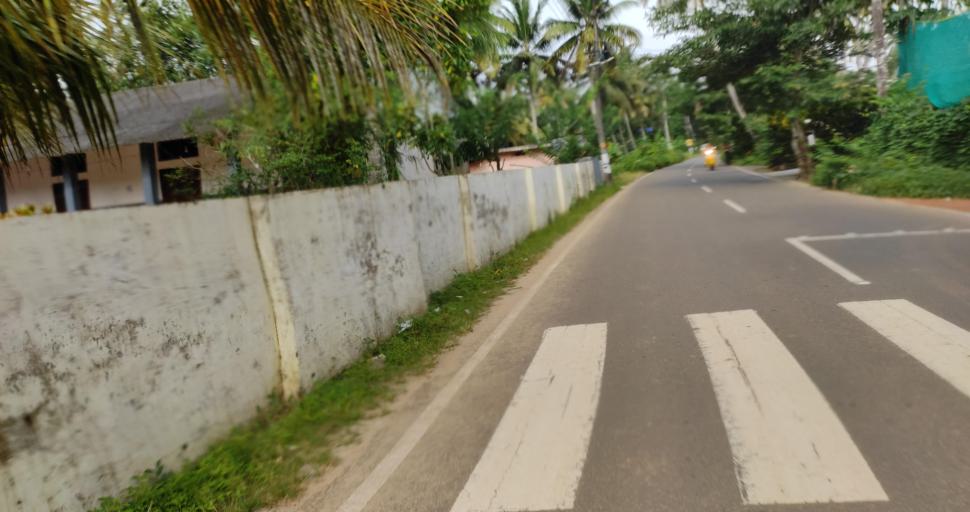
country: IN
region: Kerala
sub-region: Alappuzha
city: Vayalar
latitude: 9.6544
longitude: 76.3017
